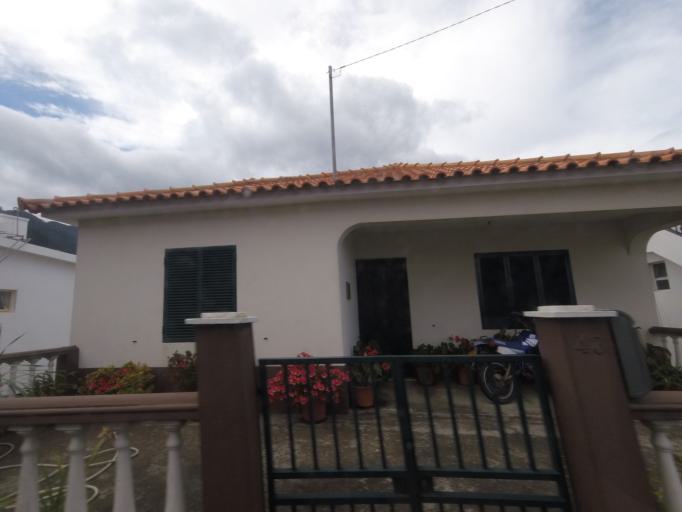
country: PT
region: Madeira
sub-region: Santana
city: Santana
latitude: 32.7624
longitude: -16.8273
